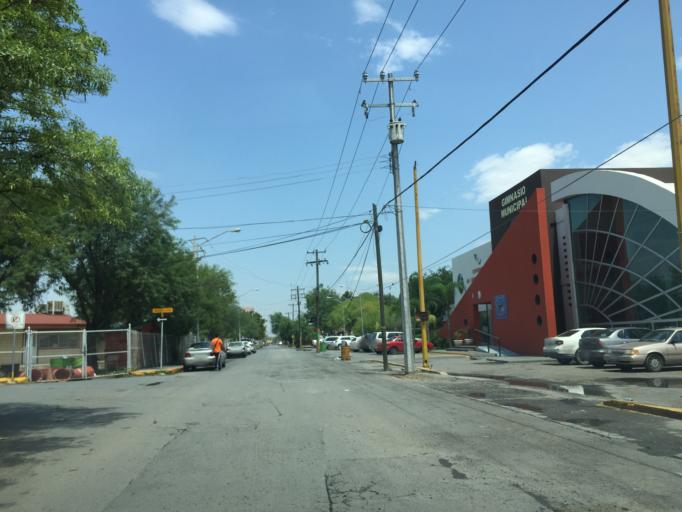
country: MX
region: Nuevo Leon
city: Apodaca
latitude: 25.7824
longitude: -100.1818
